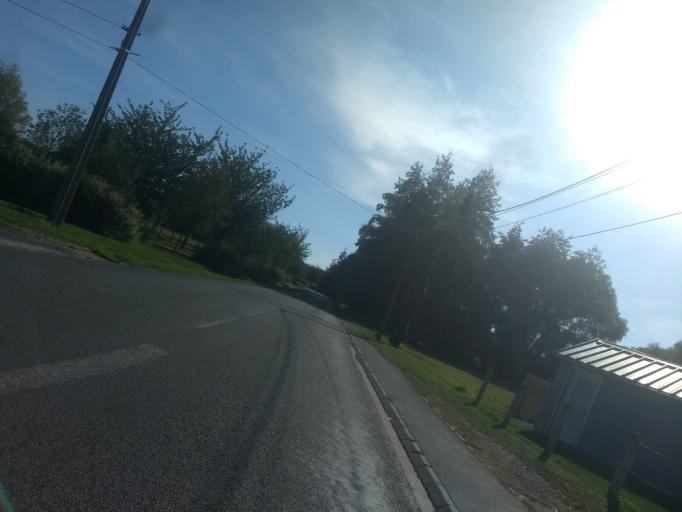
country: FR
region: Nord-Pas-de-Calais
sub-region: Departement du Pas-de-Calais
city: Roeux
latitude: 50.2913
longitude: 2.9000
